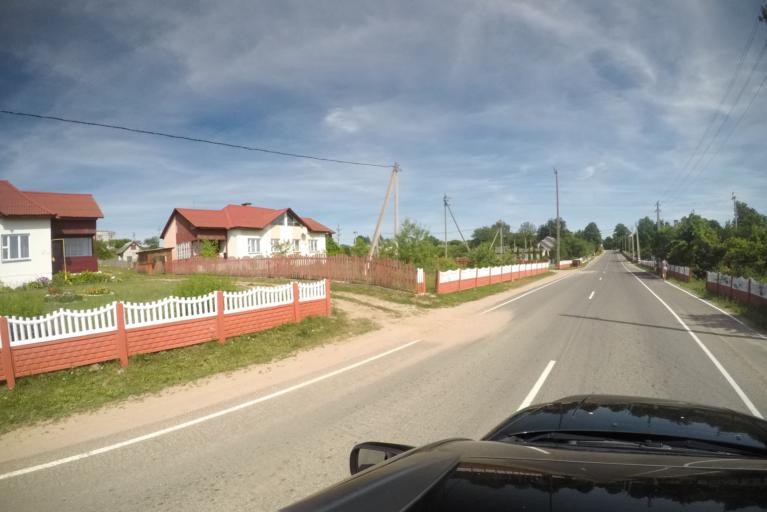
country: BY
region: Grodnenskaya
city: Hal'shany
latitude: 54.2547
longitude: 26.0171
